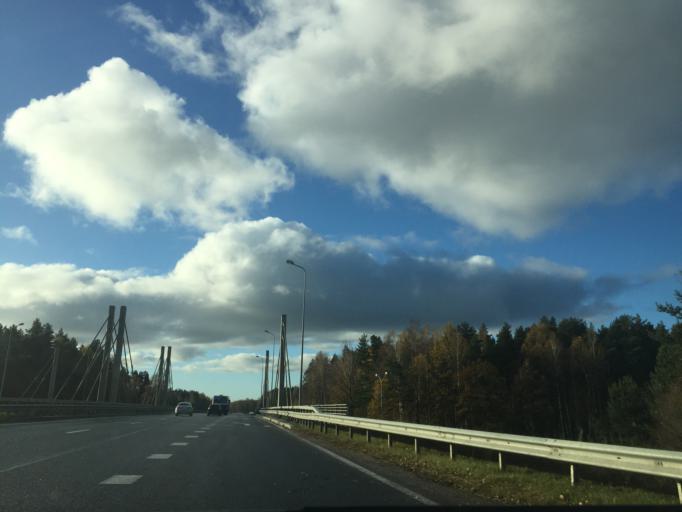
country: LV
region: Babite
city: Pinki
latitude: 56.9540
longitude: 23.9282
